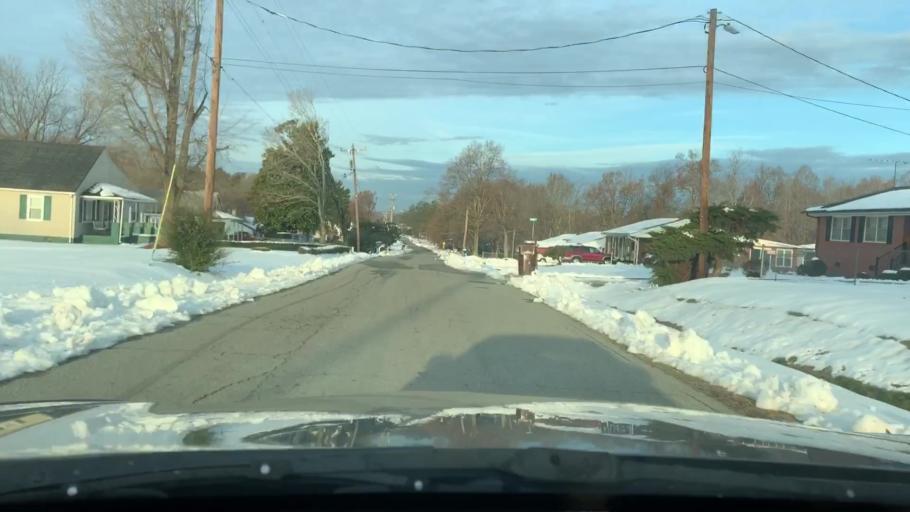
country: US
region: North Carolina
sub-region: Alamance County
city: Green Level
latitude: 36.1215
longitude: -79.3513
